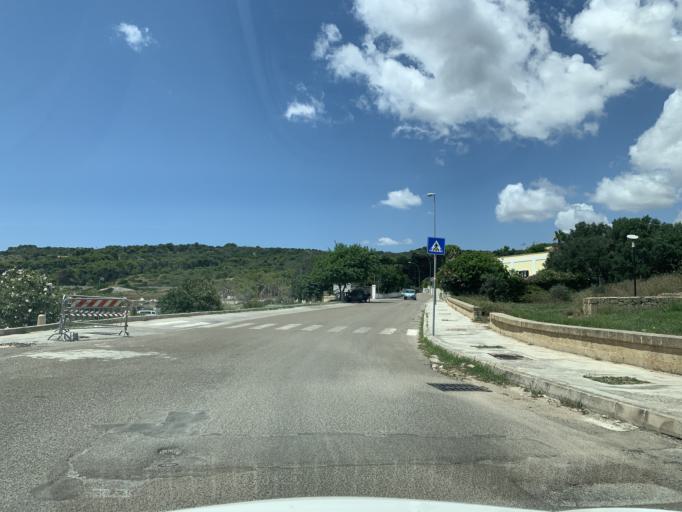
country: IT
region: Apulia
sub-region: Provincia di Lecce
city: Santa Cesarea Terme
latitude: 40.0325
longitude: 18.4490
